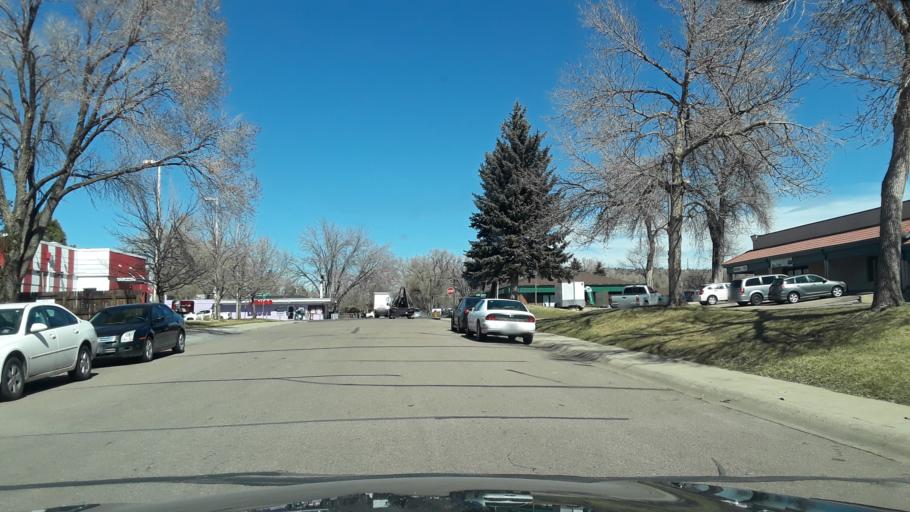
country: US
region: Colorado
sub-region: El Paso County
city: Colorado Springs
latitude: 38.8735
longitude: -104.8098
